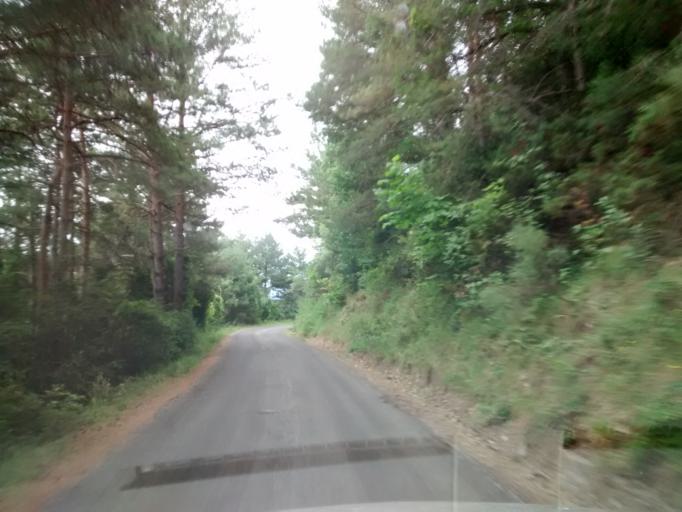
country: ES
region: Aragon
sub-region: Provincia de Huesca
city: Puertolas
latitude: 42.5660
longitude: 0.1399
